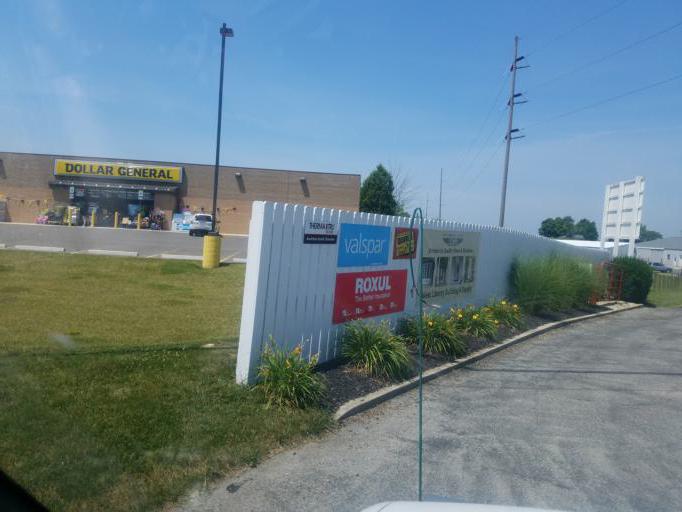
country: US
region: Ohio
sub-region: Logan County
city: West Liberty
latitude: 40.2676
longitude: -83.7607
